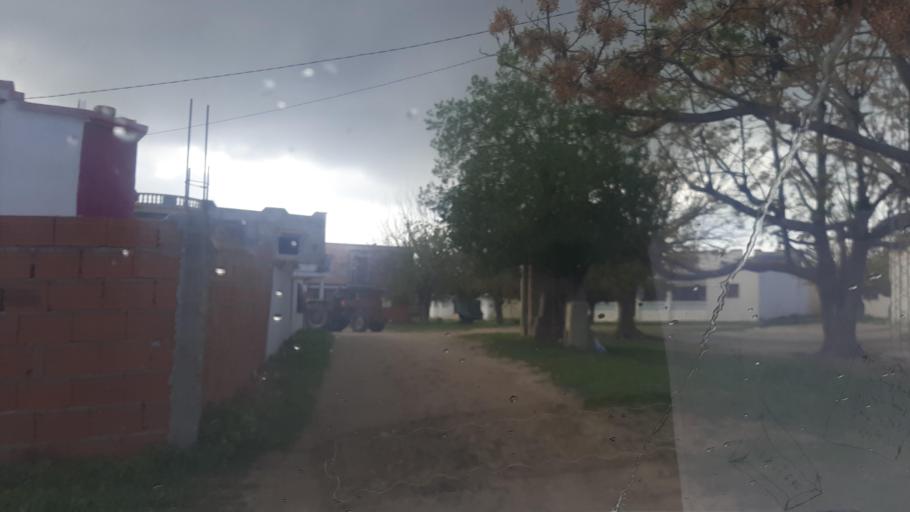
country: TN
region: Nabul
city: Manzil Bu Zalafah
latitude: 36.7351
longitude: 10.5238
